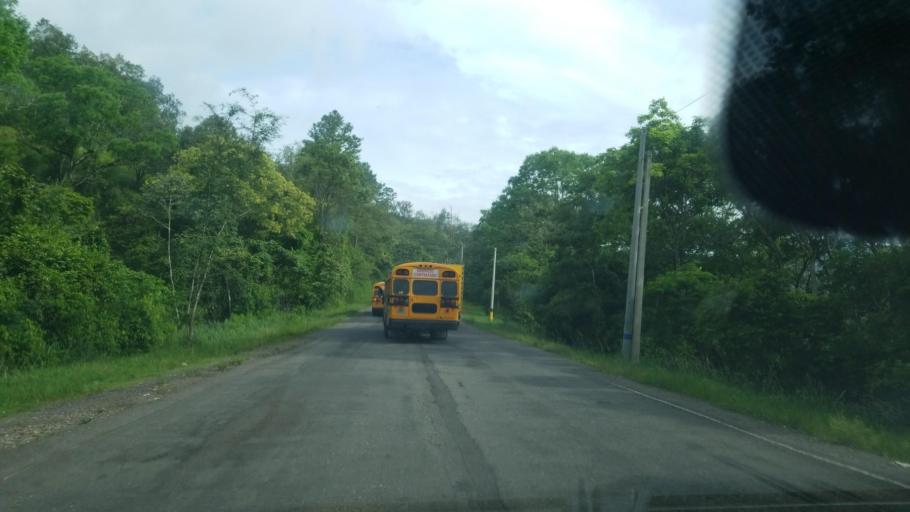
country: HN
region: Santa Barbara
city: Petoa
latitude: 15.2061
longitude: -88.2697
